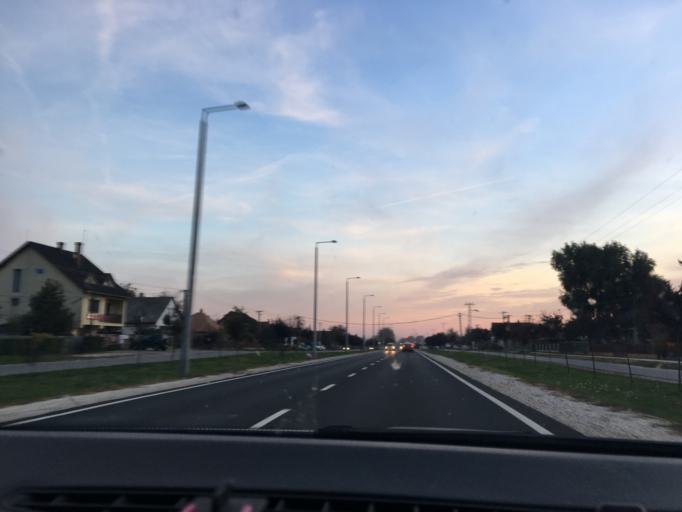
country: HU
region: Hajdu-Bihar
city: Hajduhadhaz
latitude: 47.6473
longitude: 21.6602
